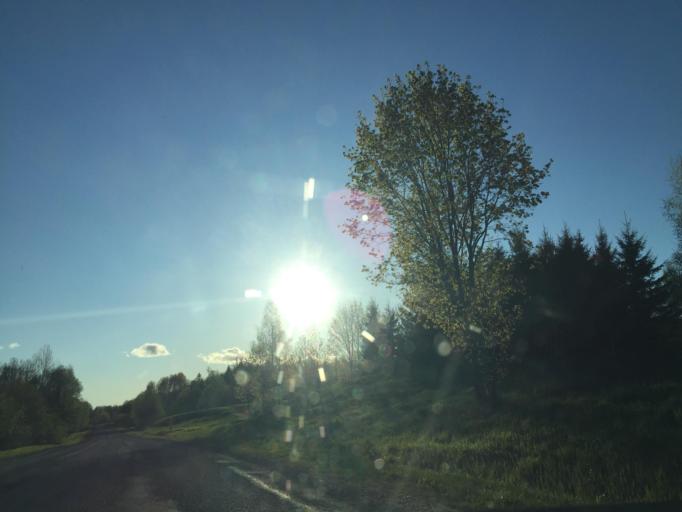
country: LV
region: Vecpiebalga
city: Vecpiebalga
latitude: 56.8414
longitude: 25.9531
